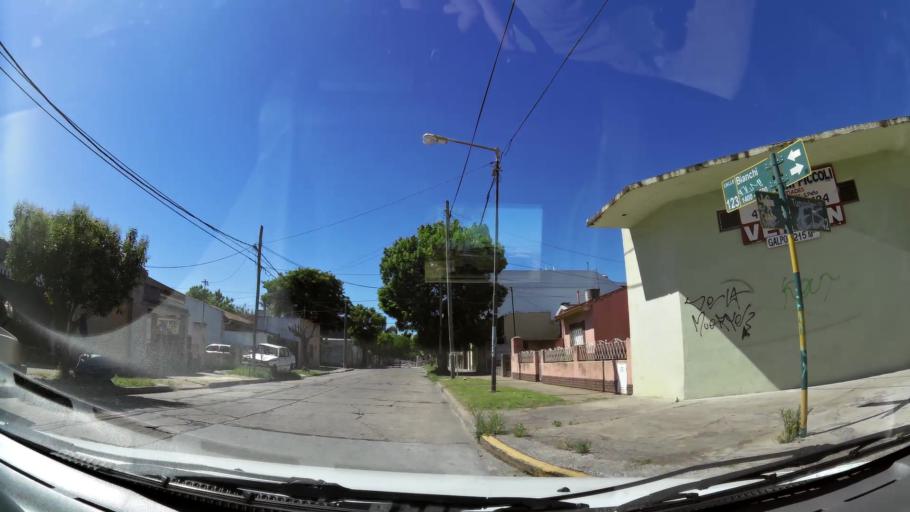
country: AR
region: Buenos Aires
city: Caseros
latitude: -34.5906
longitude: -58.5461
